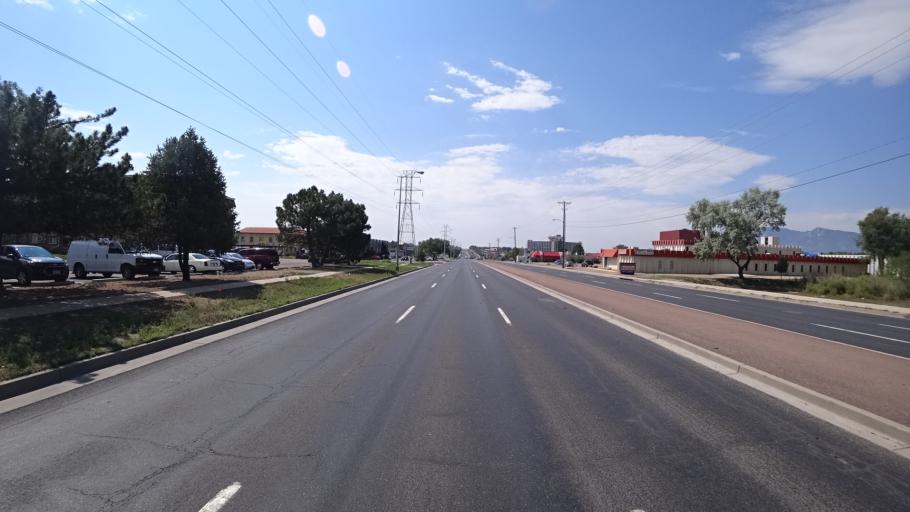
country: US
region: Colorado
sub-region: El Paso County
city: Stratmoor
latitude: 38.8293
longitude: -104.7574
